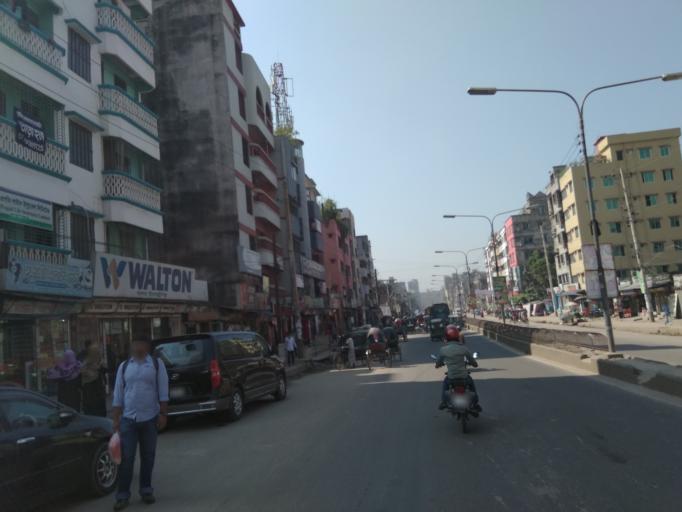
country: BD
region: Dhaka
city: Tungi
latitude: 23.8217
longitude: 90.3741
